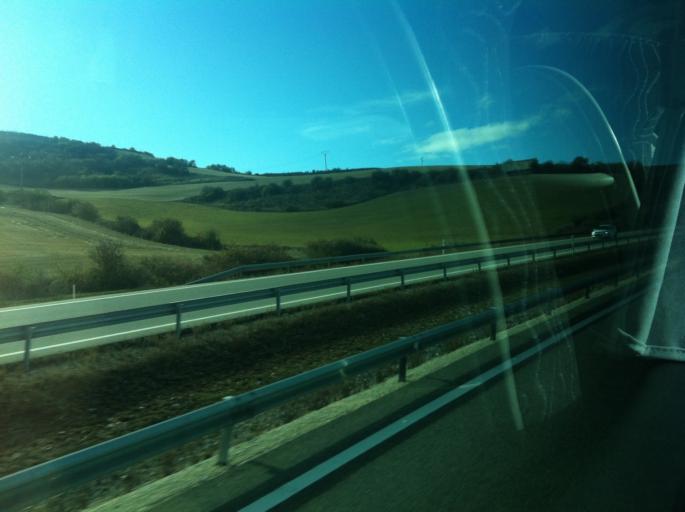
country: ES
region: Castille and Leon
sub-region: Provincia de Burgos
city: Monasterio de Rodilla
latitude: 42.4529
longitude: -3.4634
